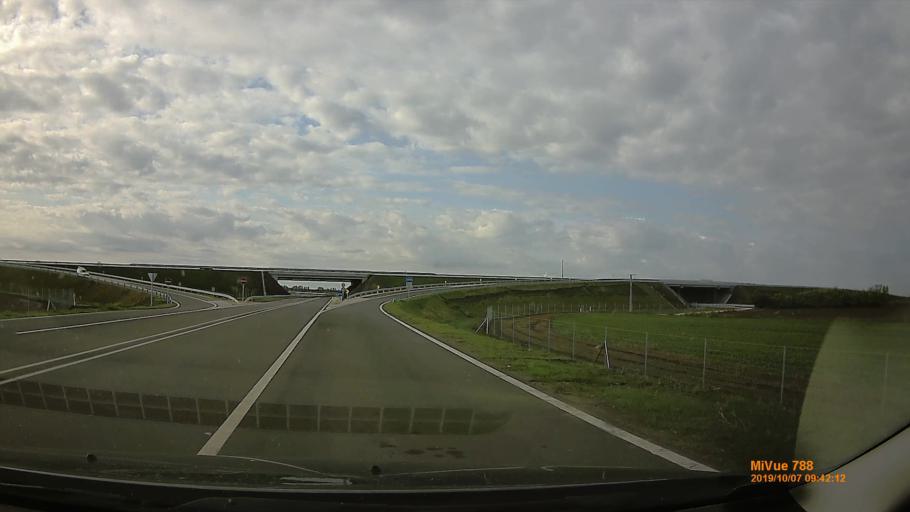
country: HU
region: Bekes
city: Nagyszenas
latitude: 46.8138
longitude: 20.6762
